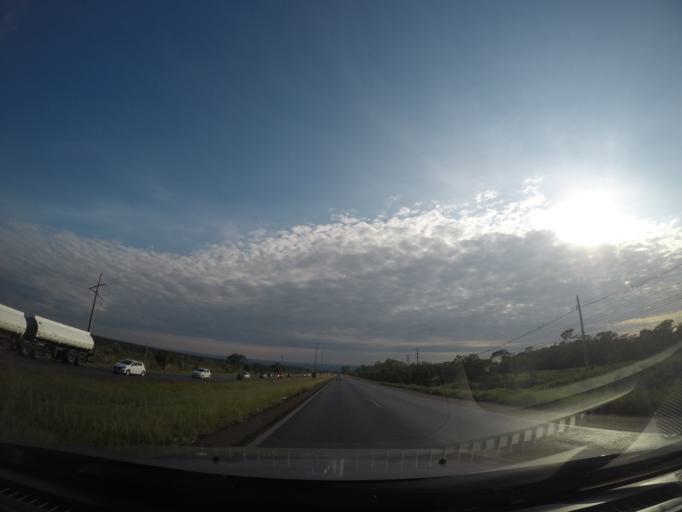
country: BR
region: Goias
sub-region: Planaltina
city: Planaltina
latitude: -15.6306
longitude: -47.7336
